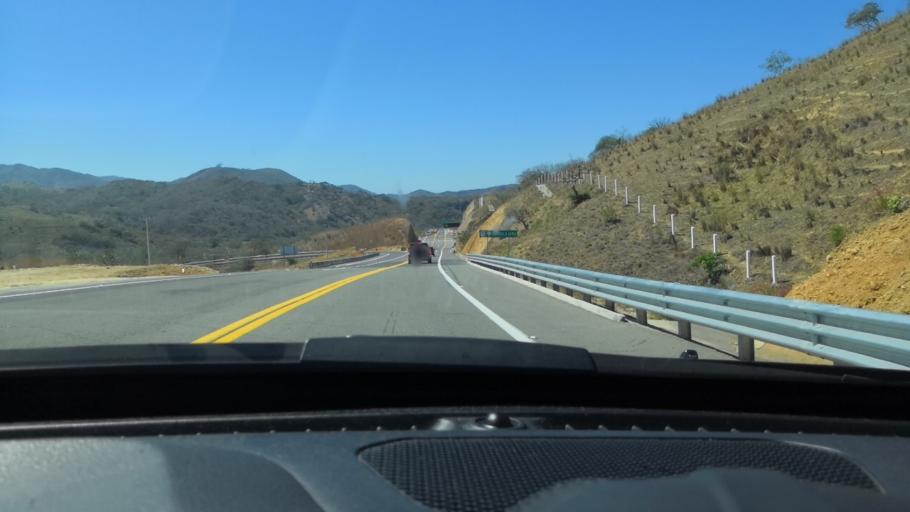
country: MX
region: Nayarit
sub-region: Compostela
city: Juan Escutia (Borbollon)
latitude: 21.1376
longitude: -104.9138
